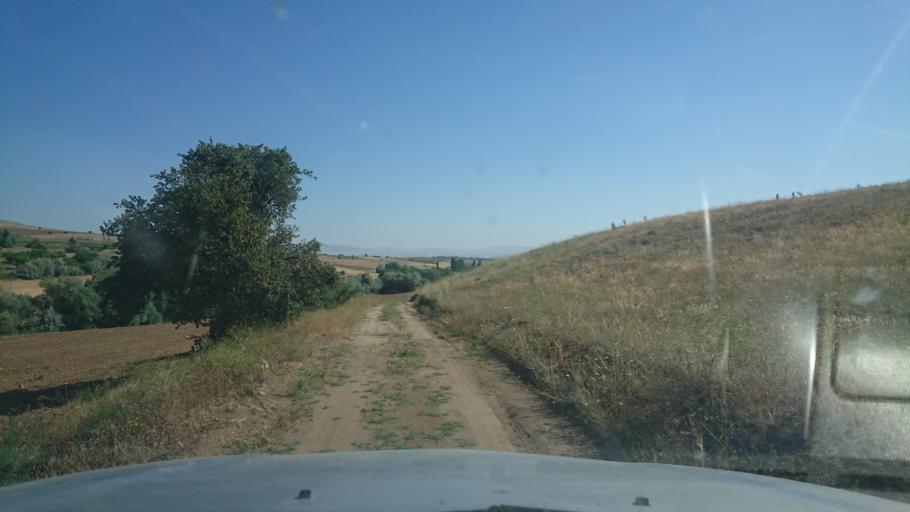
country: TR
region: Aksaray
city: Agacoren
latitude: 38.8424
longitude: 33.9259
